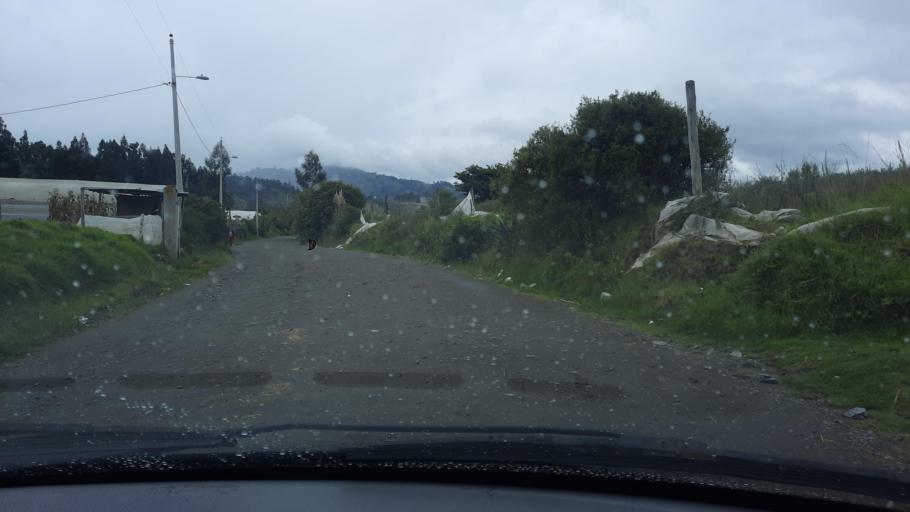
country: EC
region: Chimborazo
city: Riobamba
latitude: -1.6899
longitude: -78.6636
